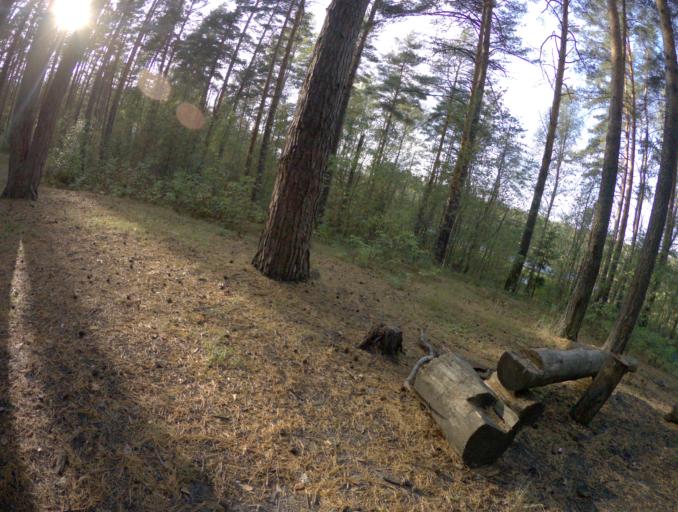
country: RU
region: Vladimir
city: Kommunar
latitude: 56.0934
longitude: 40.4700
